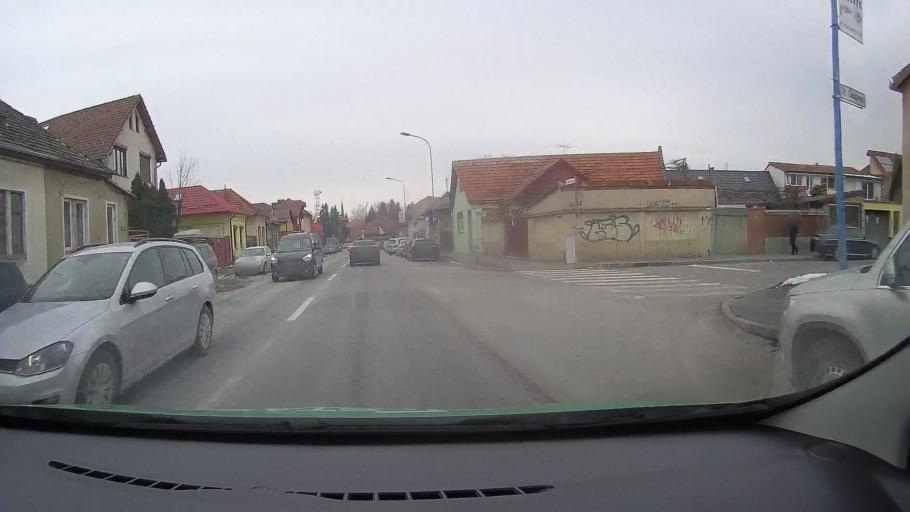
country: RO
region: Brasov
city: Brasov
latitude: 45.6605
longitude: 25.5907
